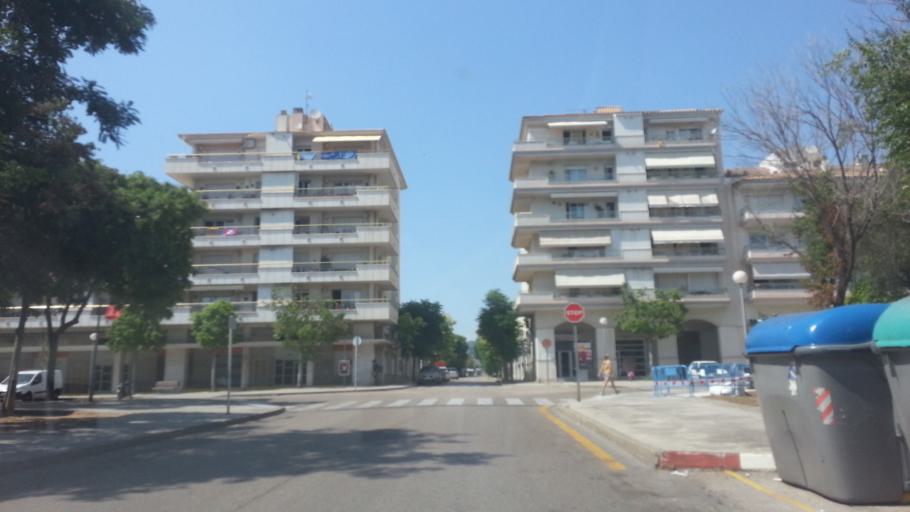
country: ES
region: Catalonia
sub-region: Provincia de Barcelona
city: Vilanova i la Geltru
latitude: 41.2235
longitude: 1.7366
